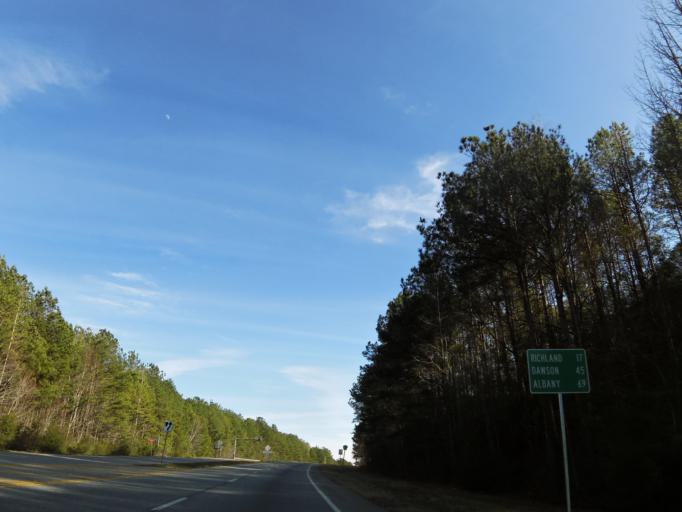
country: US
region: Georgia
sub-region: Chattahoochee County
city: Cusseta
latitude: 32.2997
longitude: -84.7793
